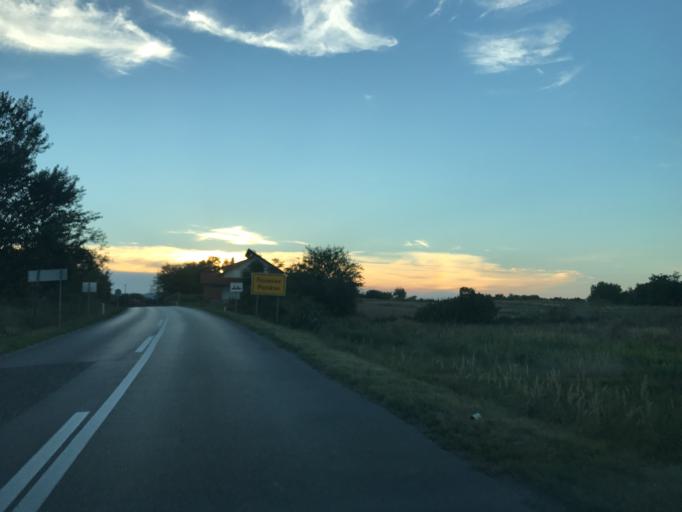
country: RS
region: Central Serbia
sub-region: Branicevski Okrug
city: Golubac
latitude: 44.6887
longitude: 21.5749
